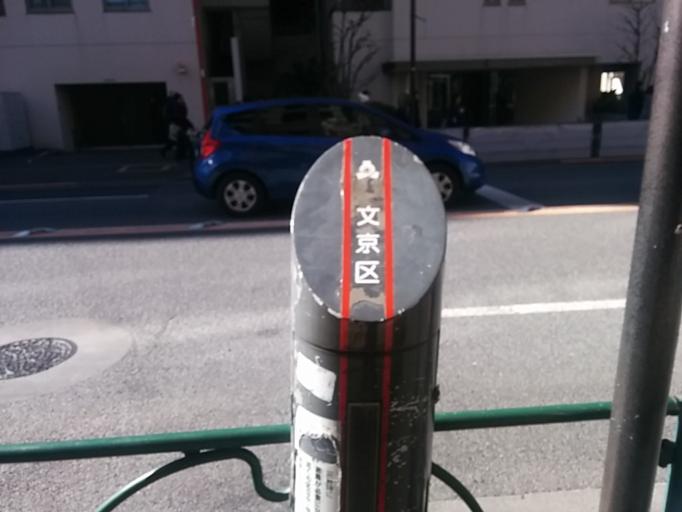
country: JP
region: Tokyo
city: Tokyo
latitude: 35.7276
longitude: 139.7635
